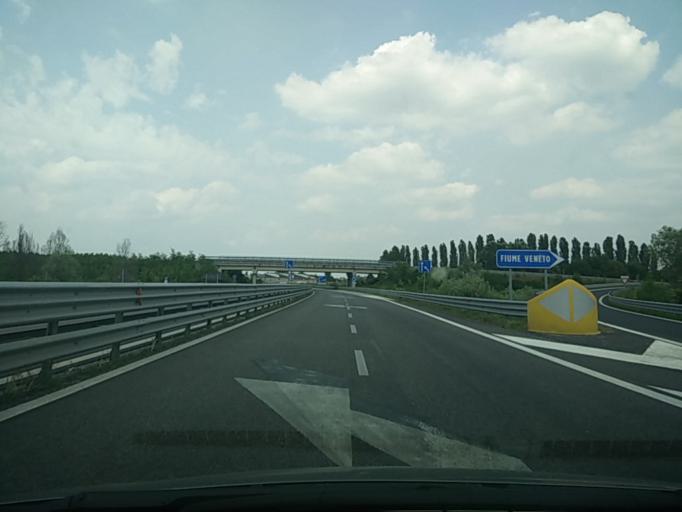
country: IT
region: Friuli Venezia Giulia
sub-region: Provincia di Pordenone
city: Fiume Veneto
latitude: 45.9371
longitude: 12.7188
